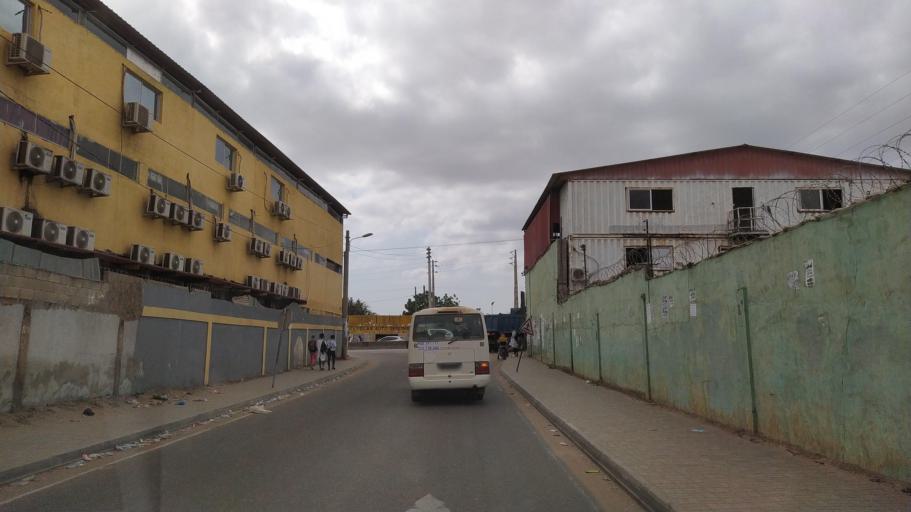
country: AO
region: Luanda
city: Luanda
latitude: -8.9640
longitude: 13.1539
